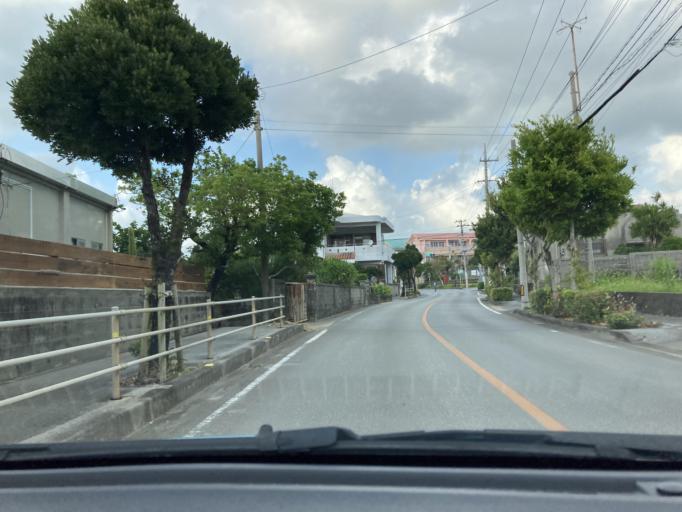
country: JP
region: Okinawa
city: Itoman
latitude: 26.0930
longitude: 127.6637
